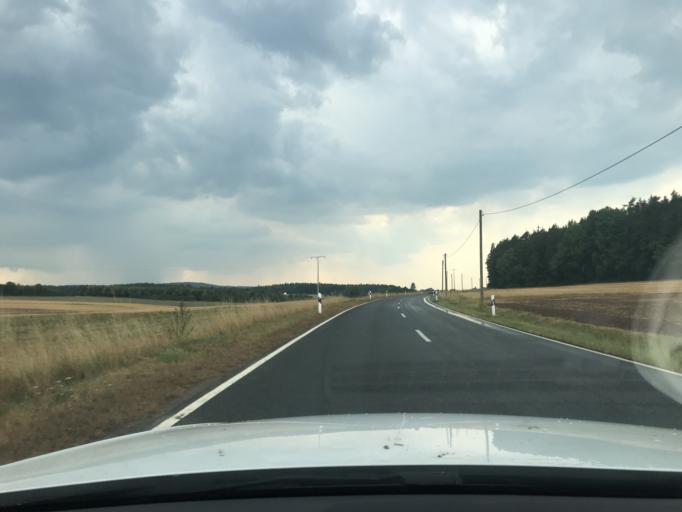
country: DE
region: Bavaria
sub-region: Upper Palatinate
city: Schlammersdorf
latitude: 49.7931
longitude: 11.7538
